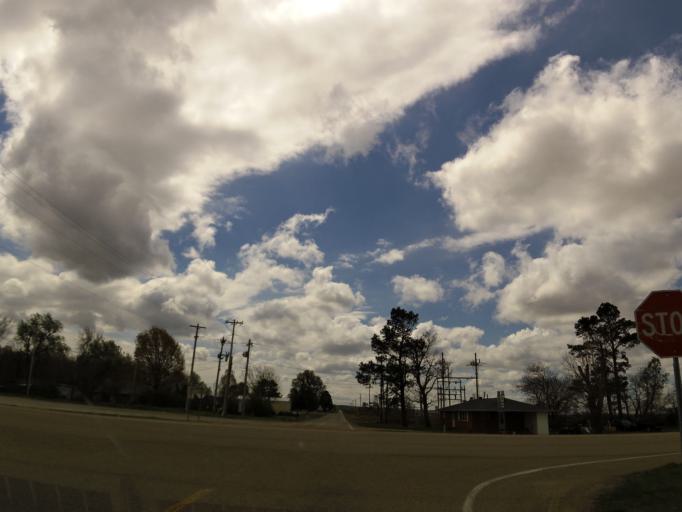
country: US
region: Arkansas
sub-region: Greene County
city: Paragould
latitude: 36.0692
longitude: -90.6725
